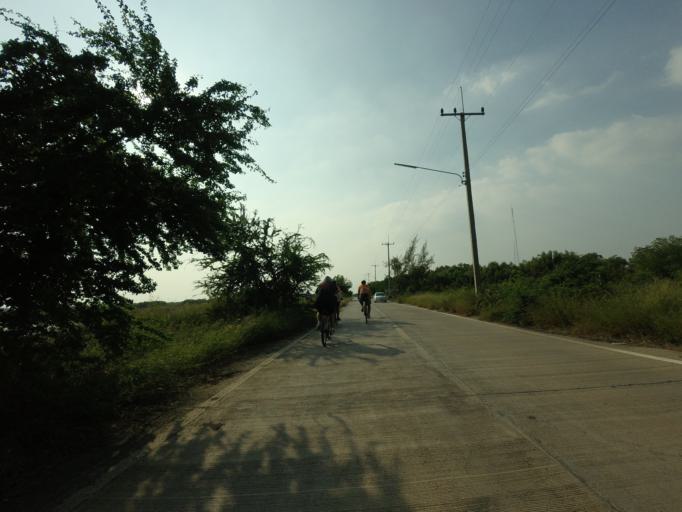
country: TH
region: Samut Sakhon
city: Samut Sakhon
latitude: 13.4982
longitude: 100.3367
